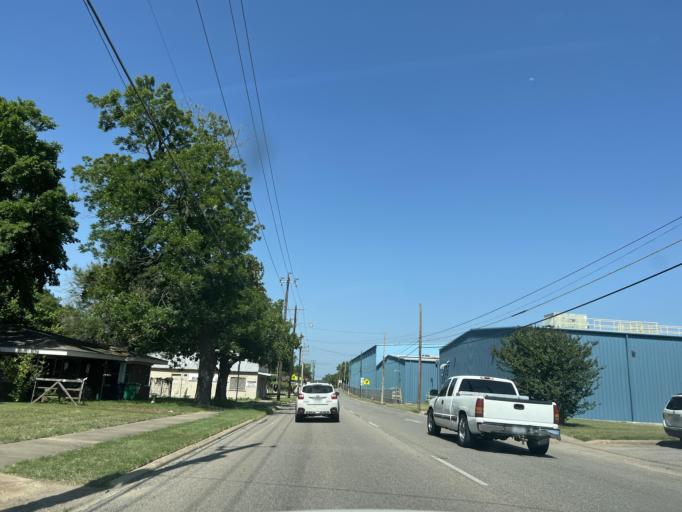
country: US
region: Texas
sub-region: Washington County
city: Brenham
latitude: 30.1679
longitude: -96.3925
